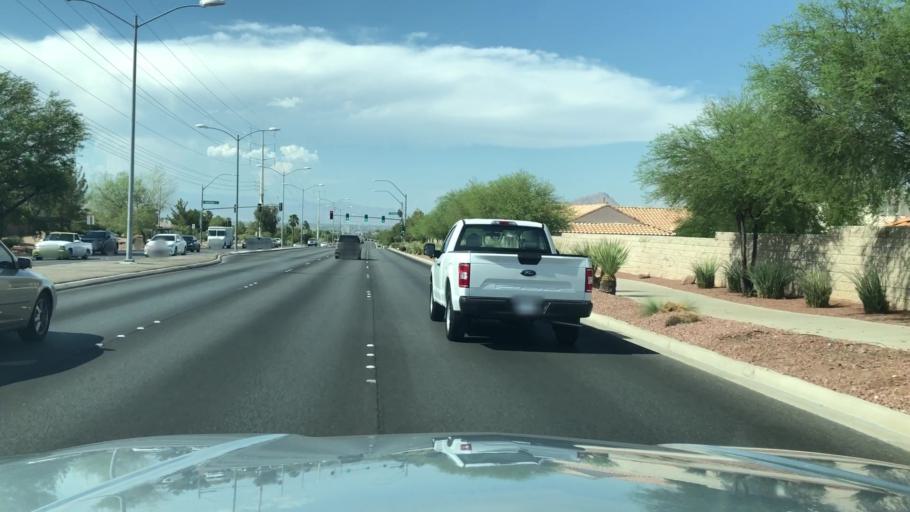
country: US
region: Nevada
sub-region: Clark County
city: Whitney
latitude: 36.0477
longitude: -115.0465
